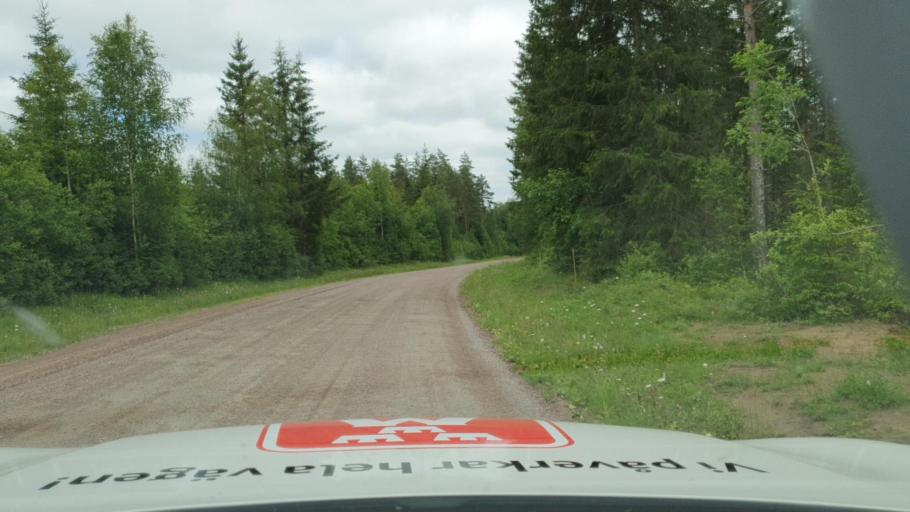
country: SE
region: Vaermland
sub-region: Filipstads Kommun
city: Filipstad
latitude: 59.6129
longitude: 13.9989
